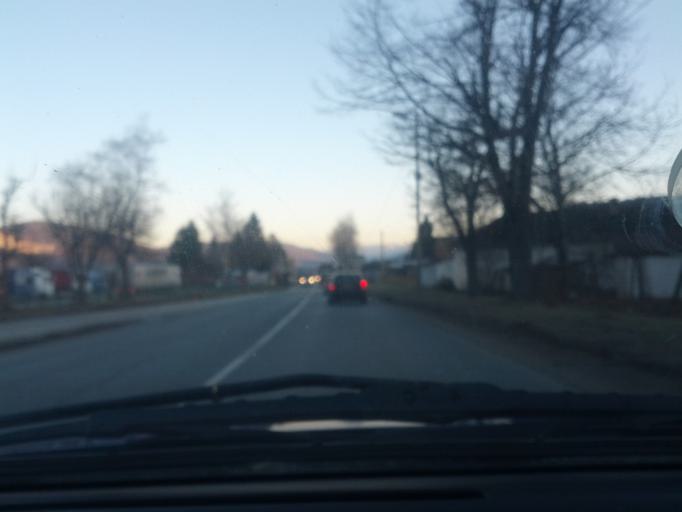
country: BG
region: Sofiya
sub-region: Obshtina Botevgrad
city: Botevgrad
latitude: 42.9783
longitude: 23.7358
